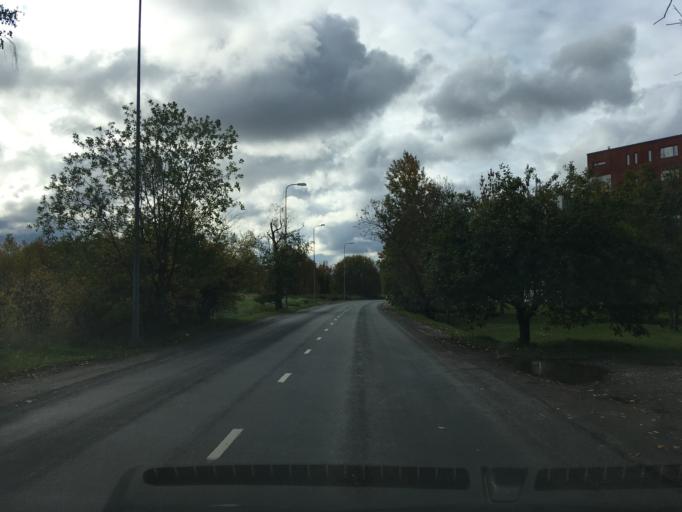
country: EE
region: Harju
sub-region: Viimsi vald
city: Viimsi
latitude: 59.4434
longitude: 24.8143
